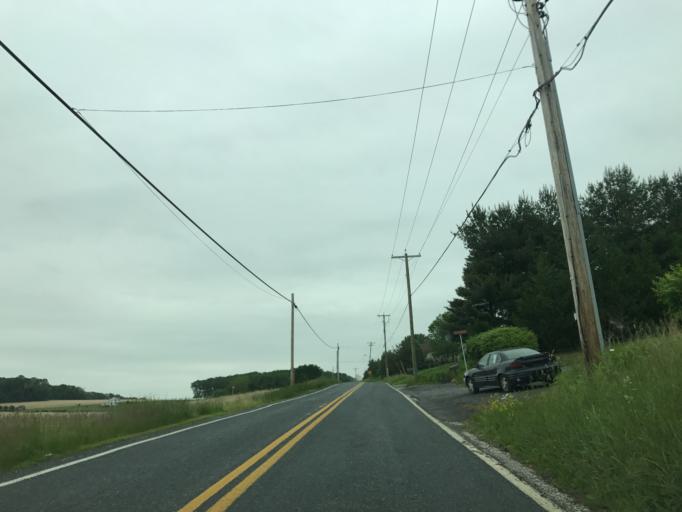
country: US
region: Pennsylvania
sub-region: York County
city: New Freedom
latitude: 39.6943
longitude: -76.7025
